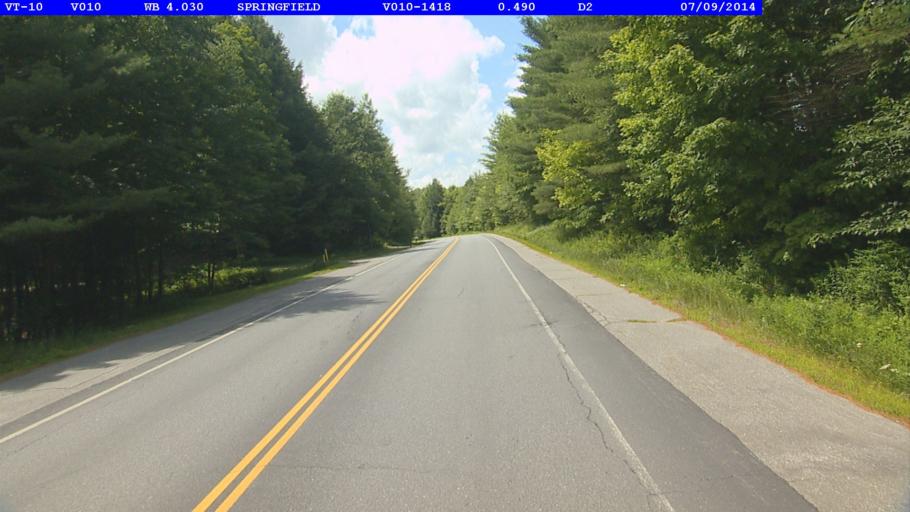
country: US
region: Vermont
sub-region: Windsor County
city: Springfield
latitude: 43.3365
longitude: -72.5375
